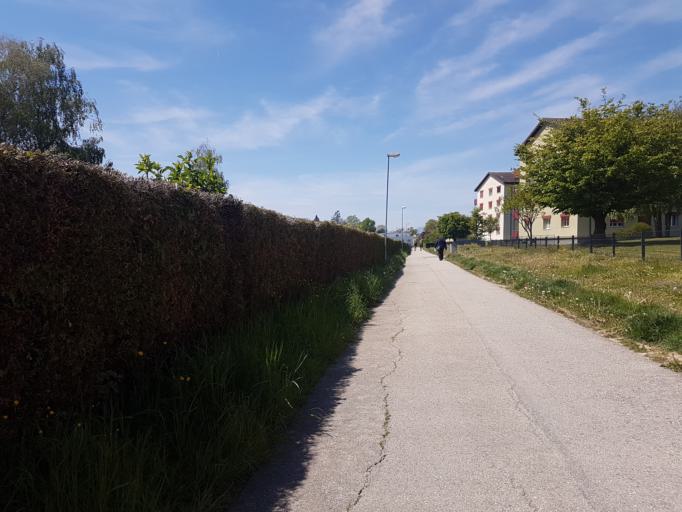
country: CH
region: Neuchatel
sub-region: Neuchatel District
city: Saint-Blaise
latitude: 47.0079
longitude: 7.0092
